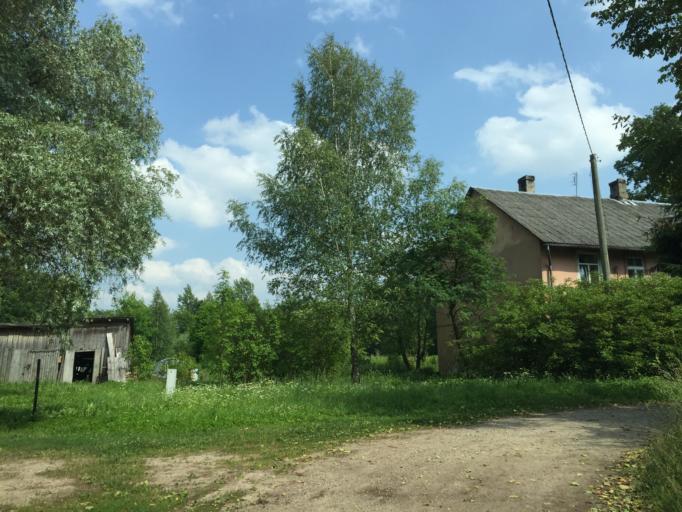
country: LV
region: Jelgava
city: Jelgava
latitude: 56.6862
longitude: 23.7207
